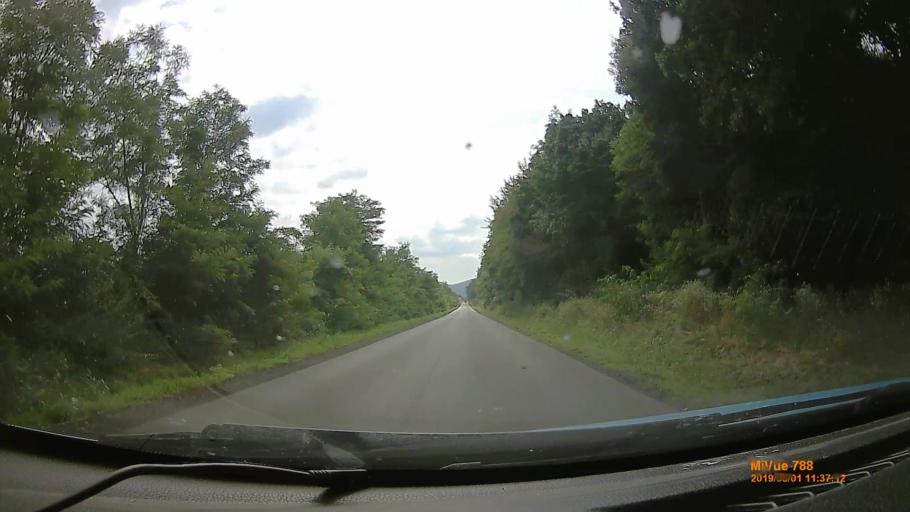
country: HU
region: Baranya
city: Villany
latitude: 45.9092
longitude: 18.3812
